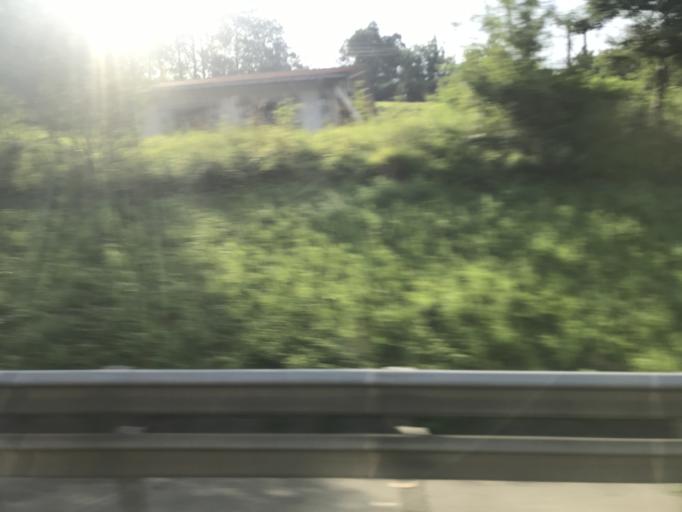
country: ES
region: Basque Country
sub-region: Provincia de Guipuzcoa
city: Villabona
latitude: 43.1820
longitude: -2.0517
